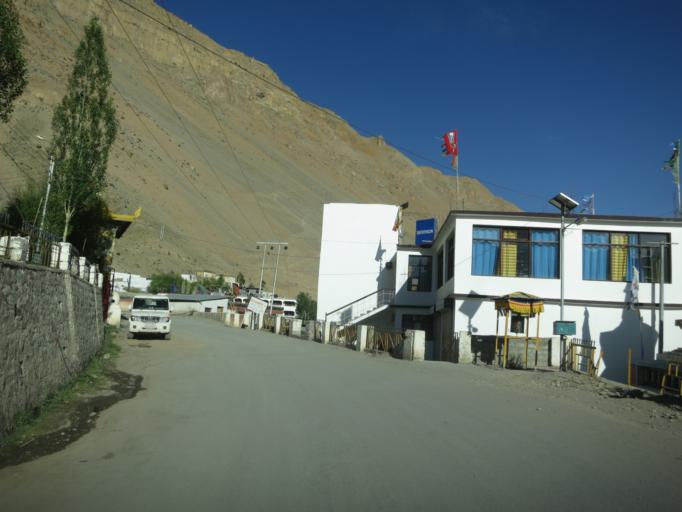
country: IN
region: Himachal Pradesh
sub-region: Shimla
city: Sarahan
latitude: 32.2277
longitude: 78.0710
